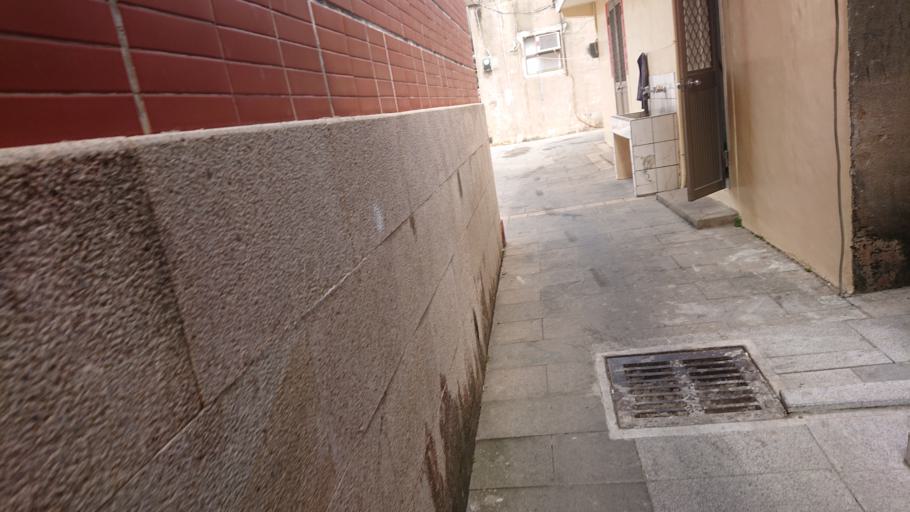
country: TW
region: Fukien
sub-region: Kinmen
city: Jincheng
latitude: 24.4283
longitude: 118.2488
